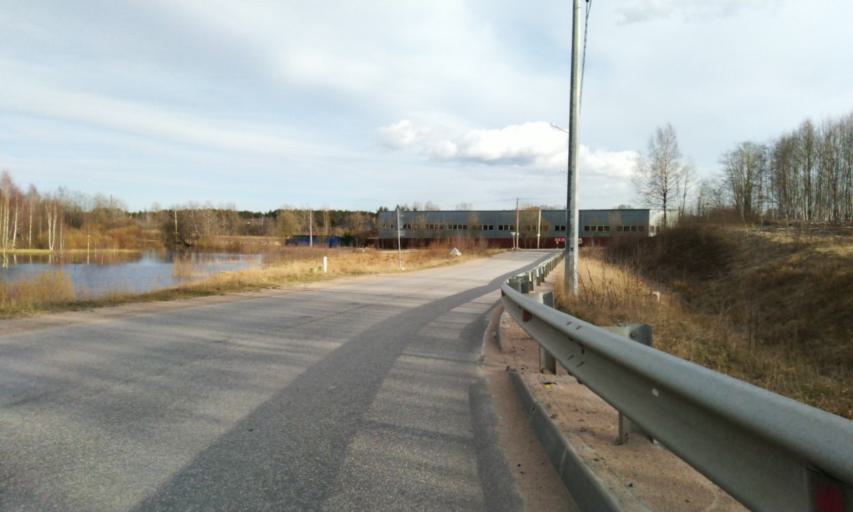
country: RU
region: Leningrad
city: Bugry
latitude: 60.1150
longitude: 30.4290
